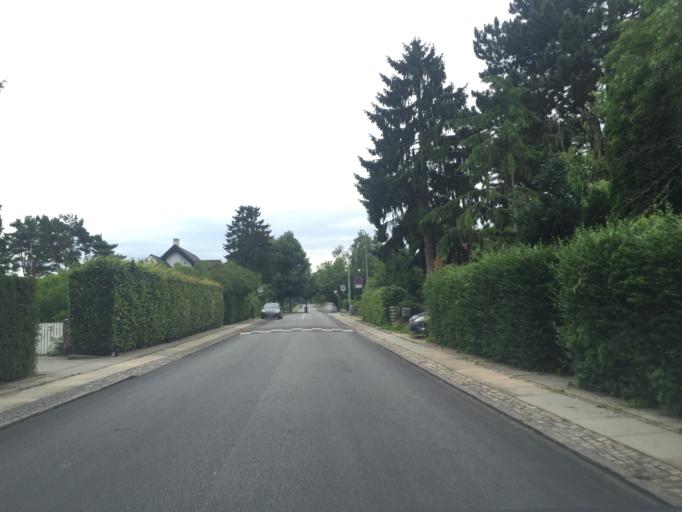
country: DK
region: Capital Region
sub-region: Lyngby-Tarbaek Kommune
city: Kongens Lyngby
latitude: 55.7885
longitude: 12.5418
